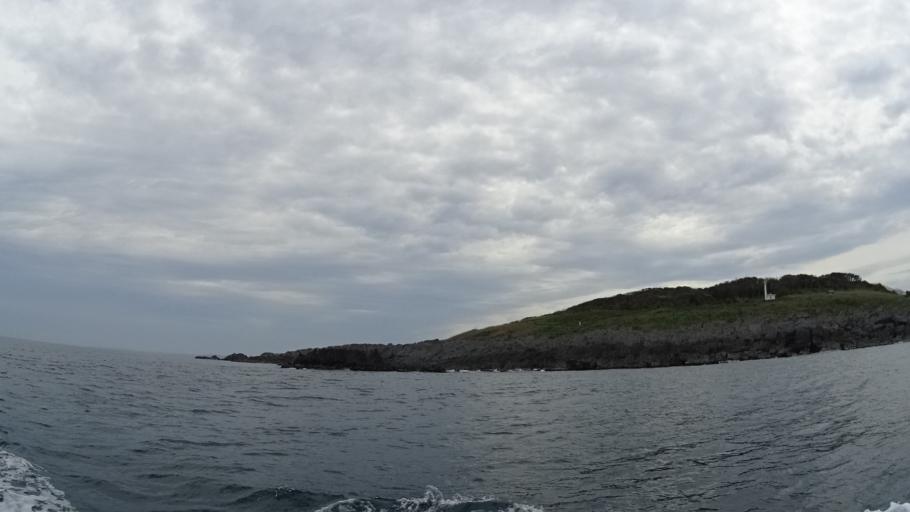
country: JP
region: Fukui
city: Mikuni
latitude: 36.2528
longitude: 136.1162
